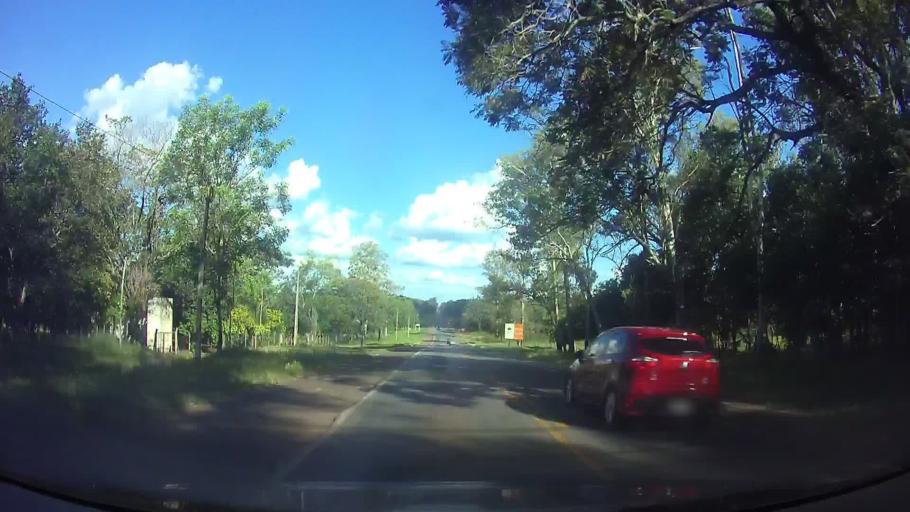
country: PY
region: Cordillera
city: Eusebio Ayala
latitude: -25.4040
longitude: -56.9440
